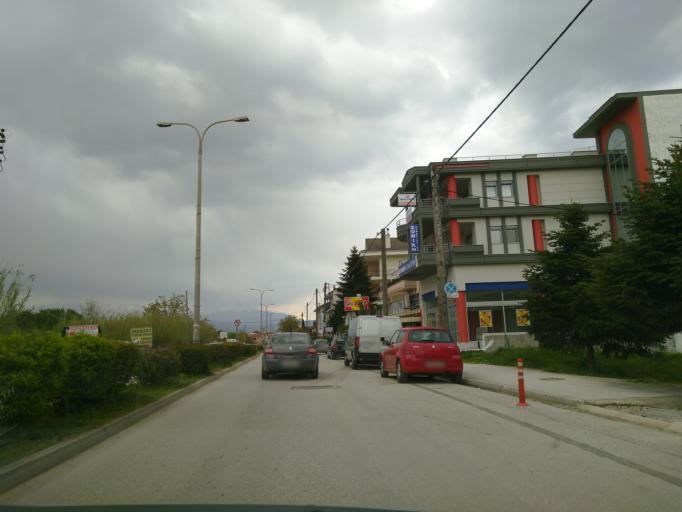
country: GR
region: Epirus
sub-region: Nomos Ioanninon
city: Ioannina
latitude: 39.6726
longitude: 20.8503
